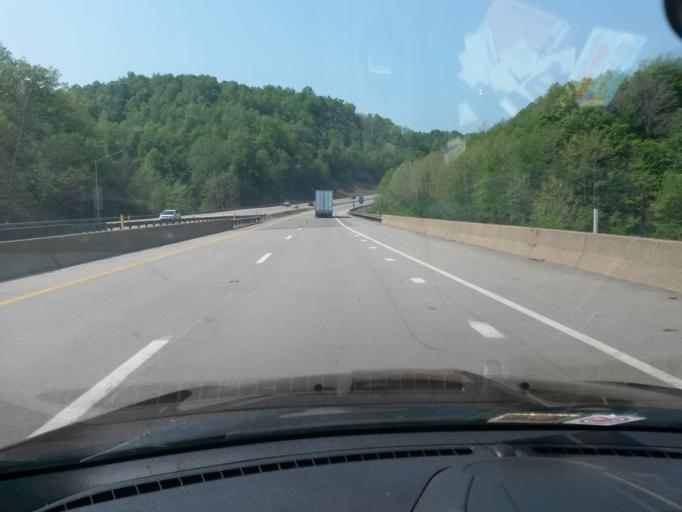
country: US
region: West Virginia
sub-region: Lewis County
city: Weston
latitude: 39.0197
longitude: -80.4294
